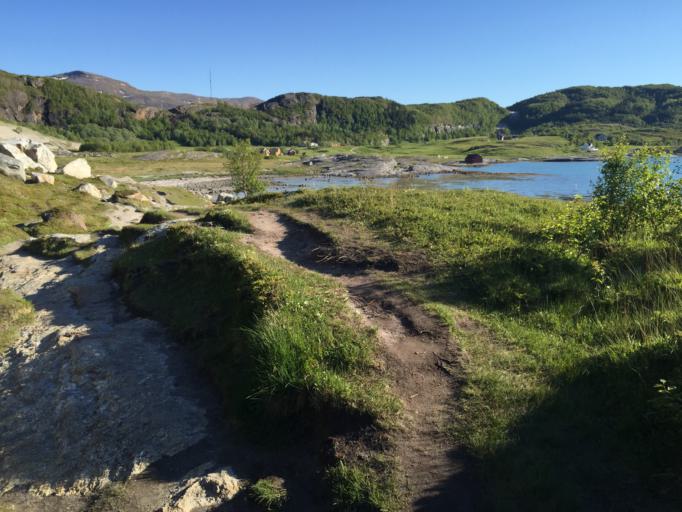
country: NO
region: Nordland
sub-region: Bodo
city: Loding
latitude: 67.4154
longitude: 14.6327
